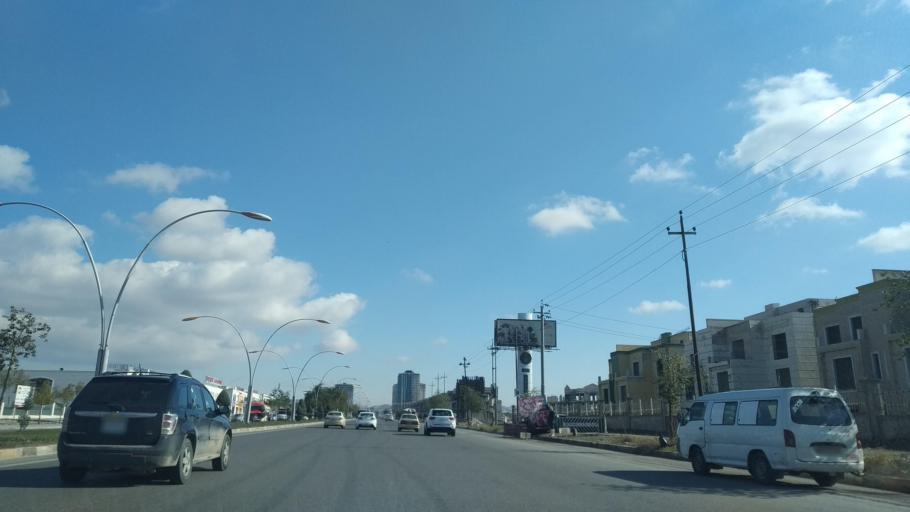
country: IQ
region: Arbil
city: Erbil
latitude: 36.2028
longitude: 44.1069
